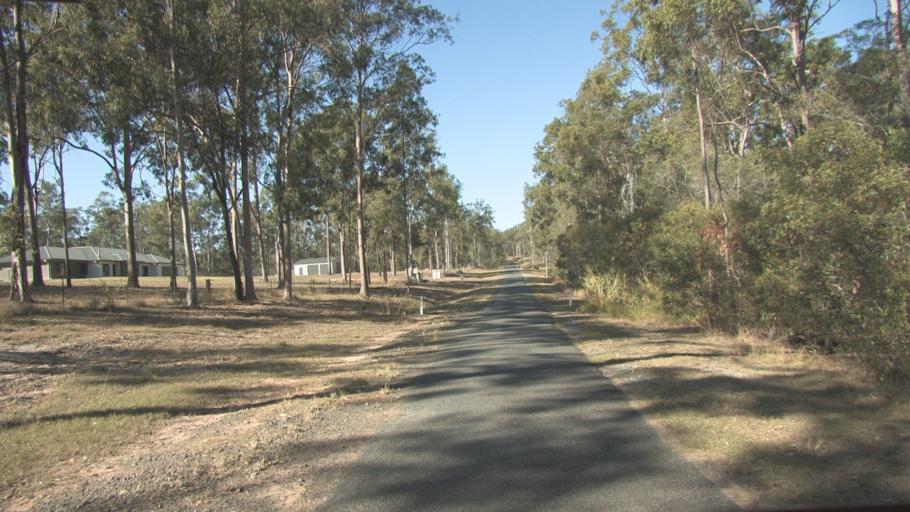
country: AU
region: Queensland
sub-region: Logan
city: Cedar Vale
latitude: -27.8397
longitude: 153.0672
